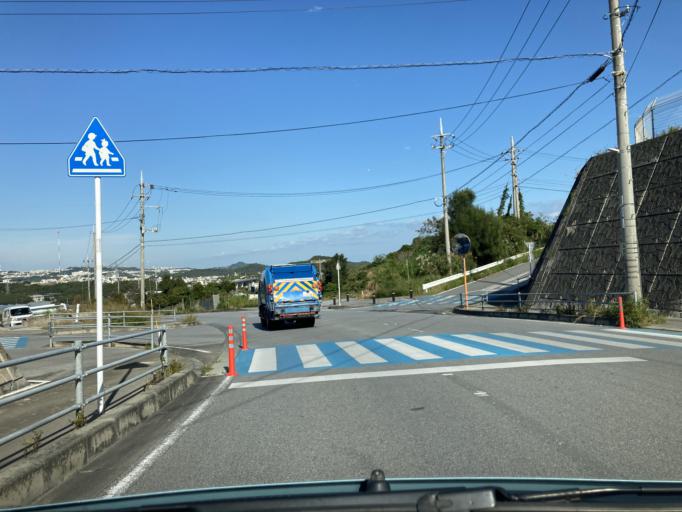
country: JP
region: Okinawa
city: Tomigusuku
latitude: 26.1685
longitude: 127.6977
